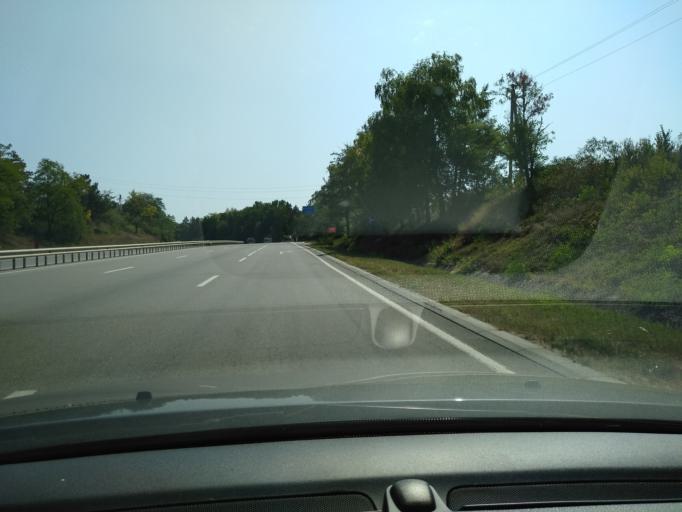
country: MD
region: Chisinau
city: Cricova
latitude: 47.1168
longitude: 28.8567
